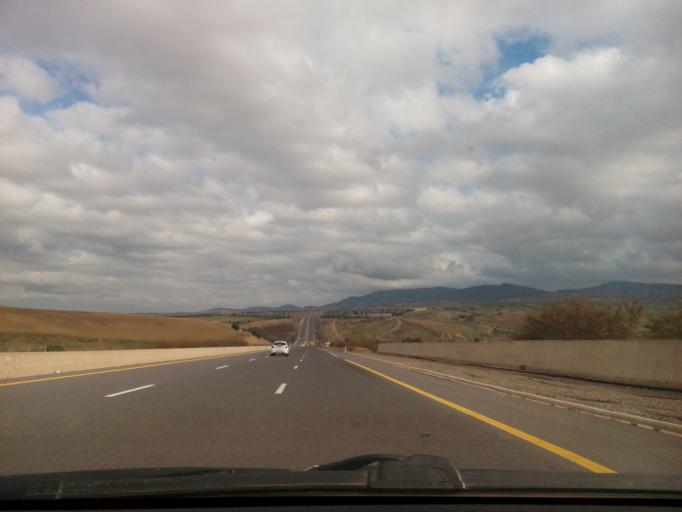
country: DZ
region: Tlemcen
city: Chetouane
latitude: 34.9799
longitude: -1.2476
